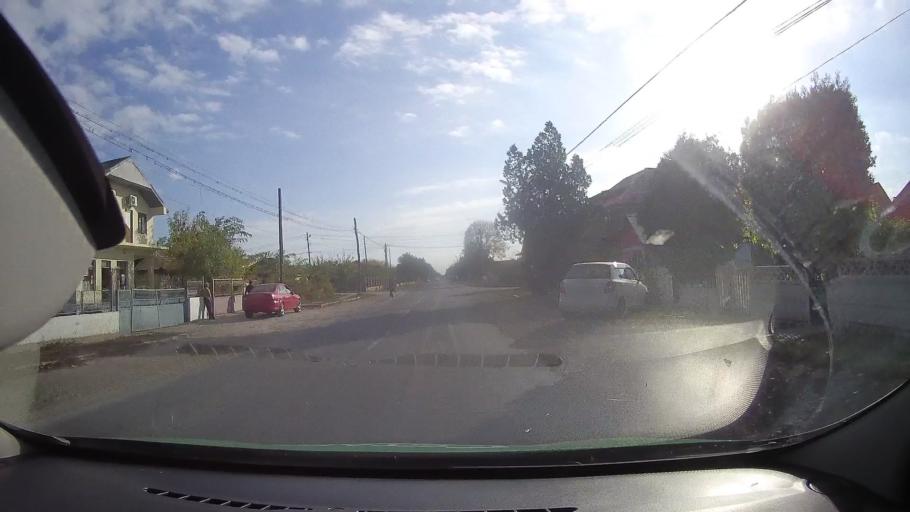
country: RO
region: Constanta
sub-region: Comuna Corbu
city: Corbu
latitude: 44.3930
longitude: 28.6619
